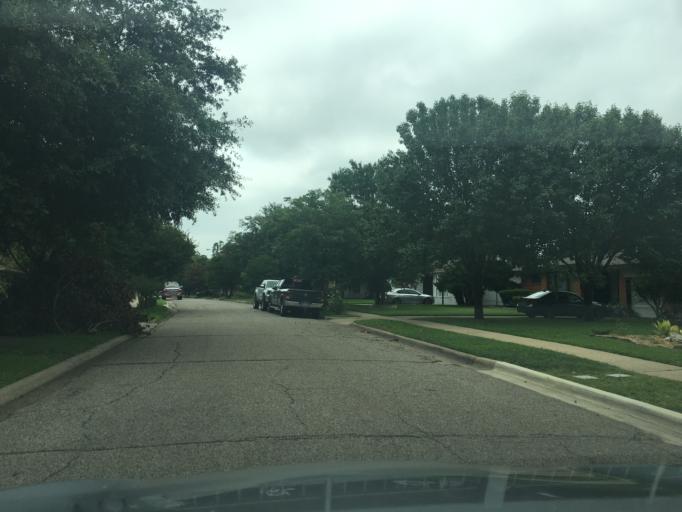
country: US
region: Texas
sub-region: Dallas County
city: Richardson
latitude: 32.9482
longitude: -96.7472
